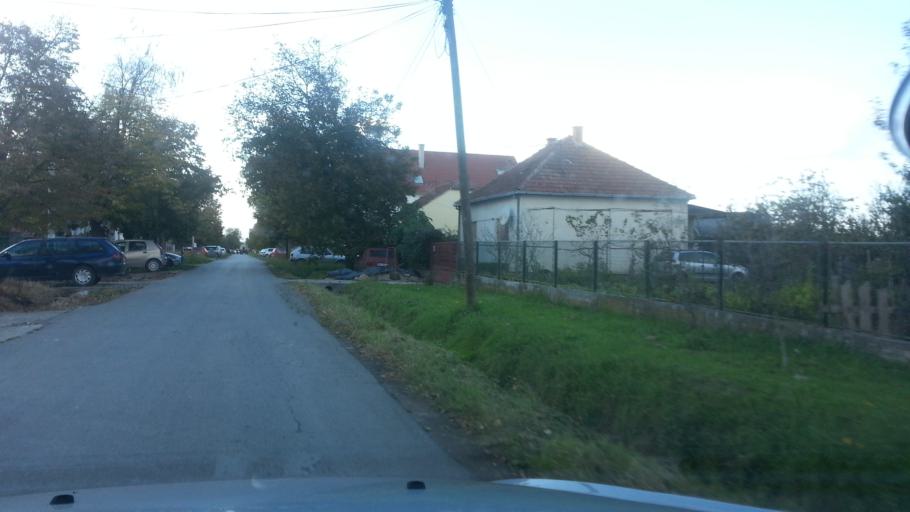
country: RS
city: Novi Banovci
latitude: 44.9073
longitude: 20.2669
